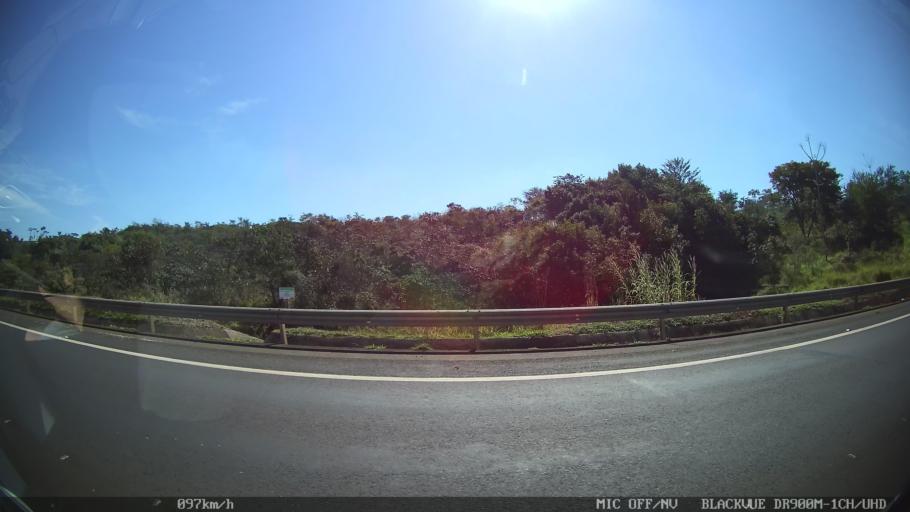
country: BR
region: Sao Paulo
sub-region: Franca
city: Franca
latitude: -20.5565
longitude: -47.4363
